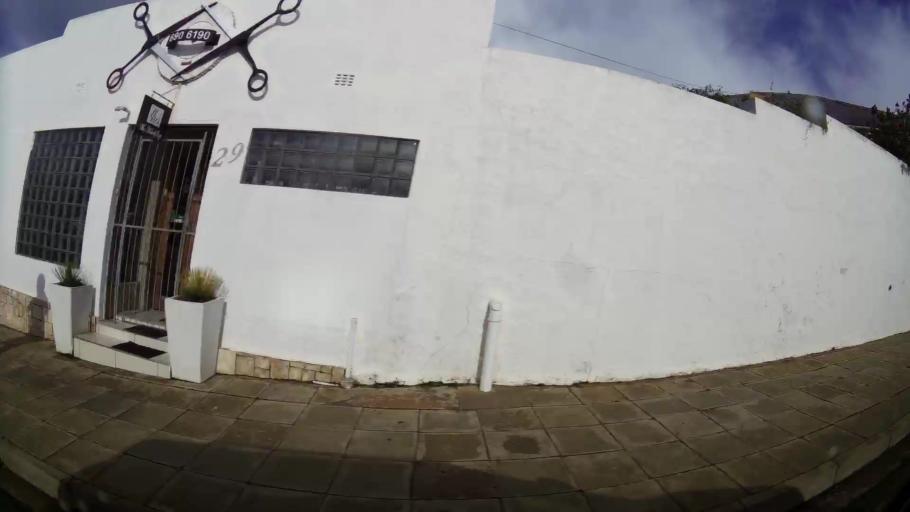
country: ZA
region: Western Cape
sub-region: Eden District Municipality
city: Mossel Bay
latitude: -34.1845
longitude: 22.1419
